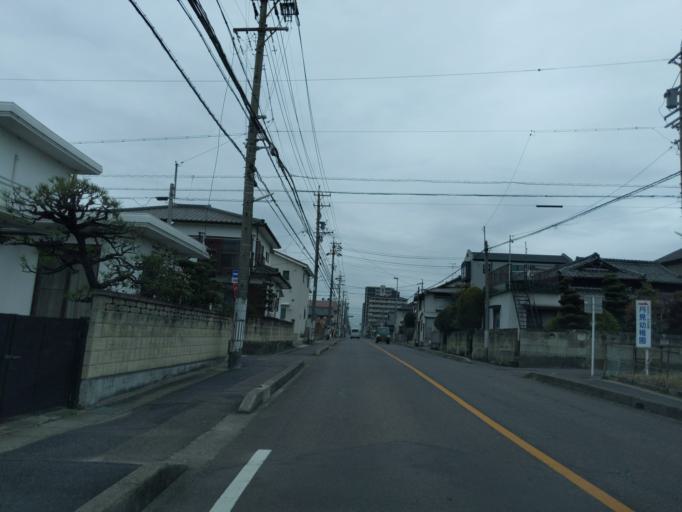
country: JP
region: Aichi
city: Kasugai
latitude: 35.2418
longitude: 136.9751
